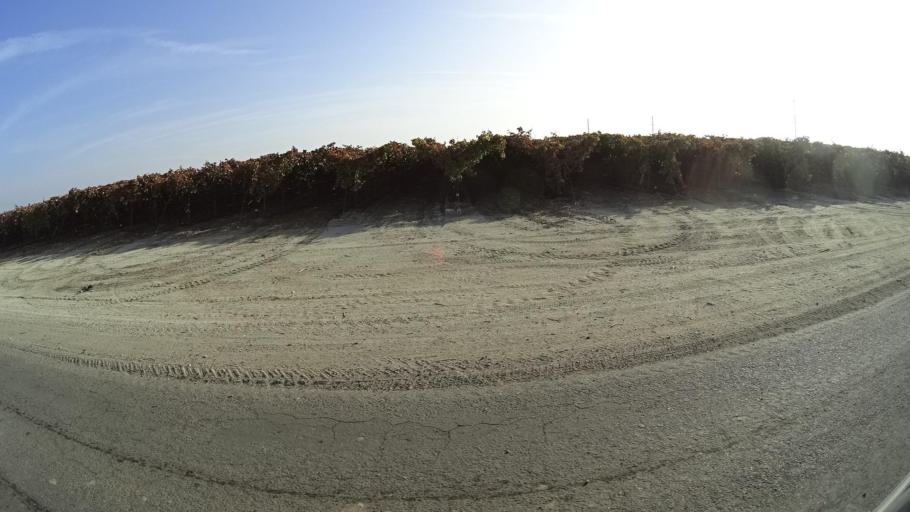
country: US
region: California
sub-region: Kern County
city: McFarland
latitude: 35.7043
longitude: -119.1871
